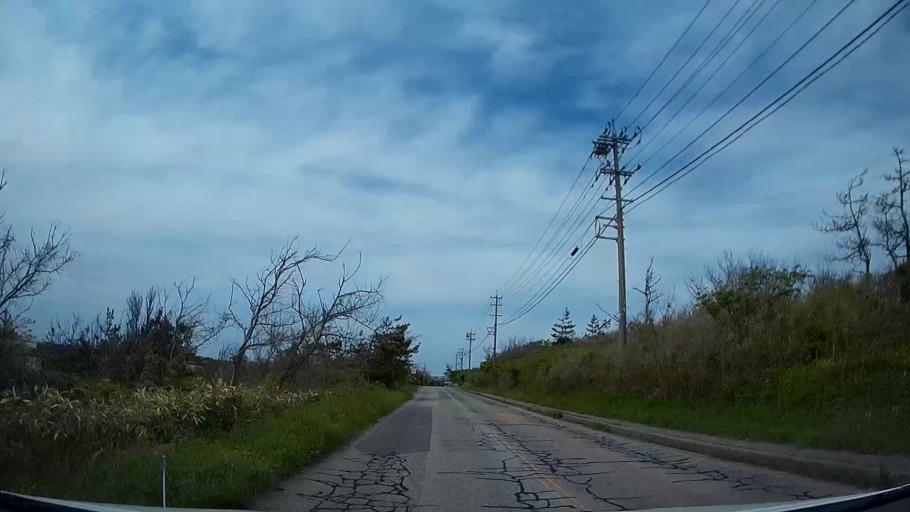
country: JP
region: Ishikawa
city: Hakui
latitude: 36.9995
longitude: 136.7703
